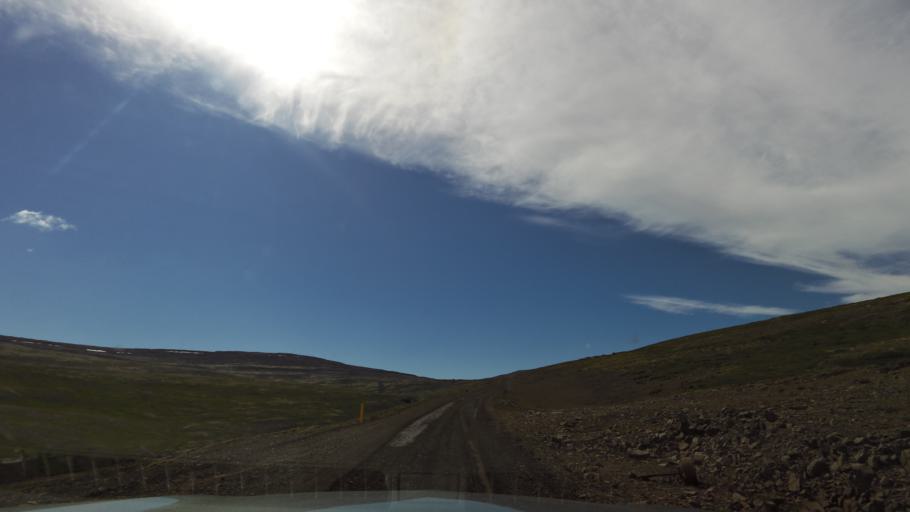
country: IS
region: West
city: Olafsvik
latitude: 65.5217
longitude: -23.9268
